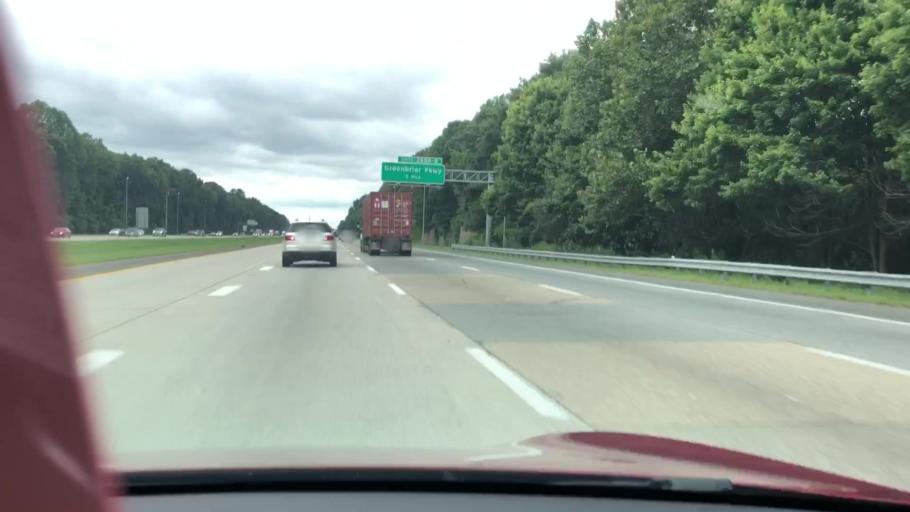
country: US
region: Virginia
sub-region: City of Chesapeake
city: Chesapeake
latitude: 36.7980
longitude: -76.2075
